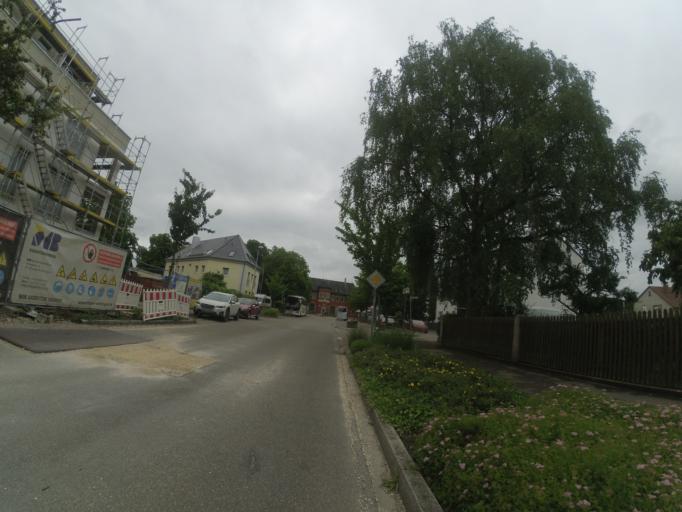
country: DE
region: Baden-Wuerttemberg
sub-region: Tuebingen Region
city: Langenau
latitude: 48.4944
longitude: 10.1251
